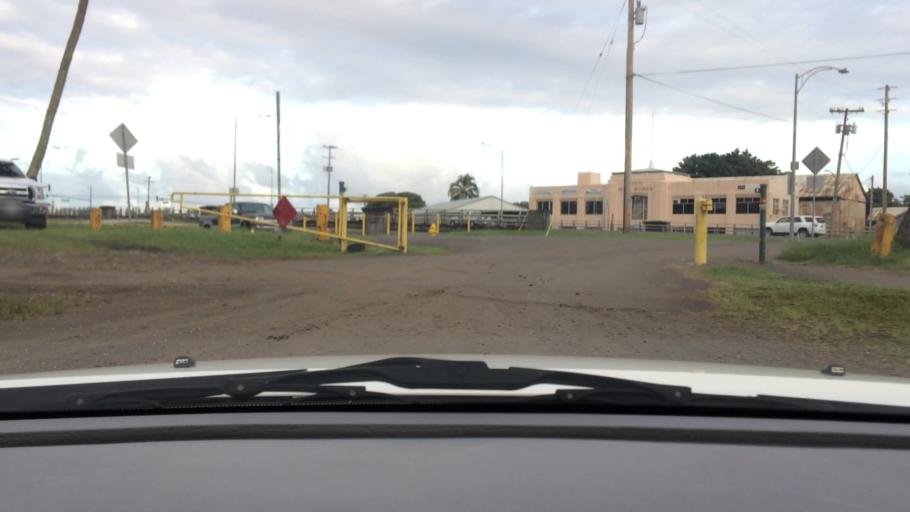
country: US
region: Hawaii
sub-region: Hawaii County
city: Hilo
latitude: 19.7229
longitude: -155.0719
